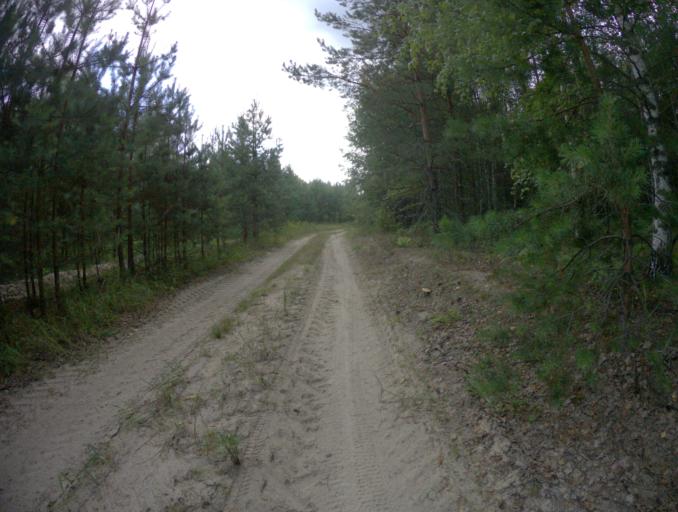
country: RU
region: Vladimir
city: Vorsha
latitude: 55.9479
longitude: 40.1457
